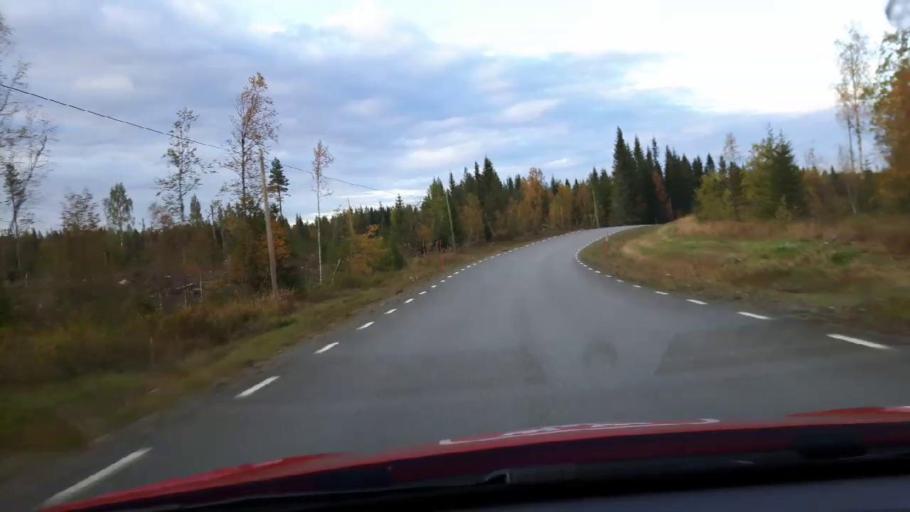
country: SE
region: Jaemtland
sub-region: OEstersunds Kommun
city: Lit
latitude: 63.3206
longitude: 15.1500
